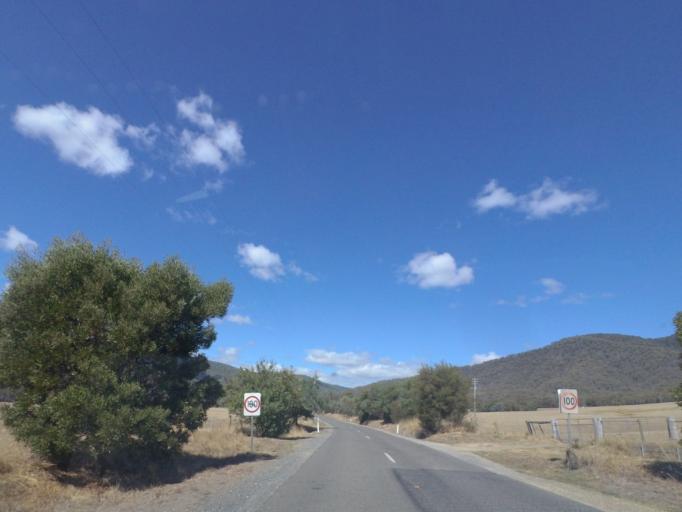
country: AU
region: Victoria
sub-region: Murrindindi
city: Alexandra
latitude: -37.2953
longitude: 145.8228
